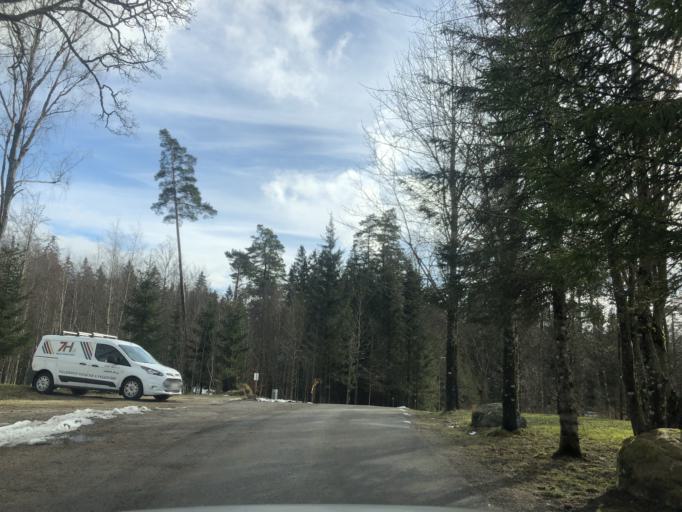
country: SE
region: Vaestra Goetaland
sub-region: Ulricehamns Kommun
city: Ulricehamn
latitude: 57.7829
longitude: 13.4395
